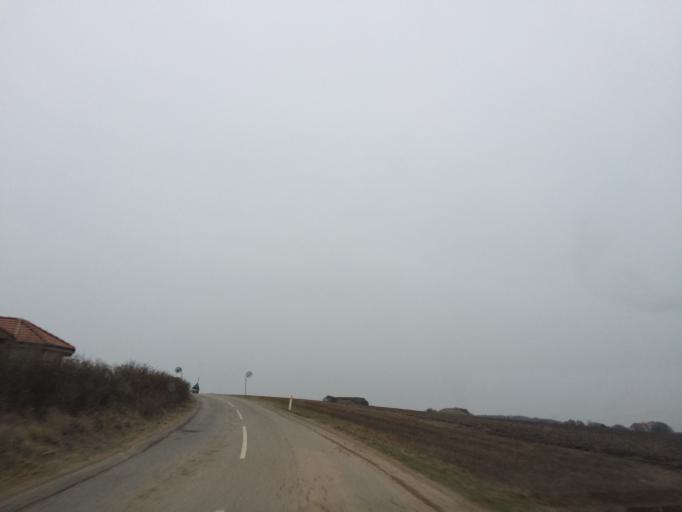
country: DK
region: Central Jutland
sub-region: Lemvig Kommune
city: Lemvig
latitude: 56.5821
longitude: 8.2753
